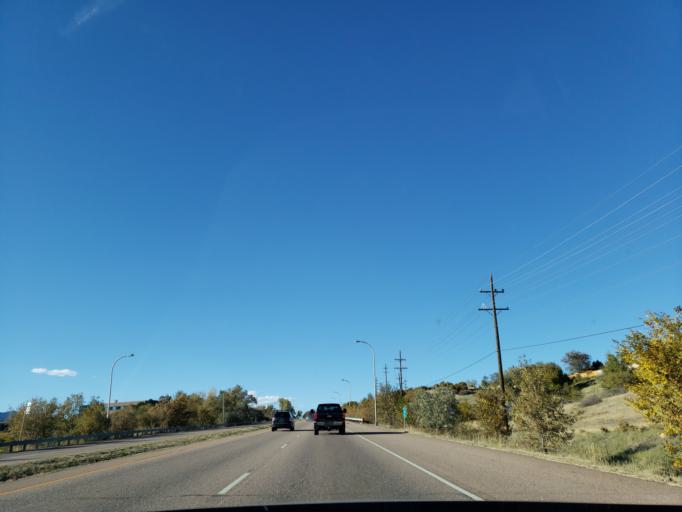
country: US
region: Colorado
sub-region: El Paso County
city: Stratmoor
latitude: 38.7811
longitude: -104.8187
